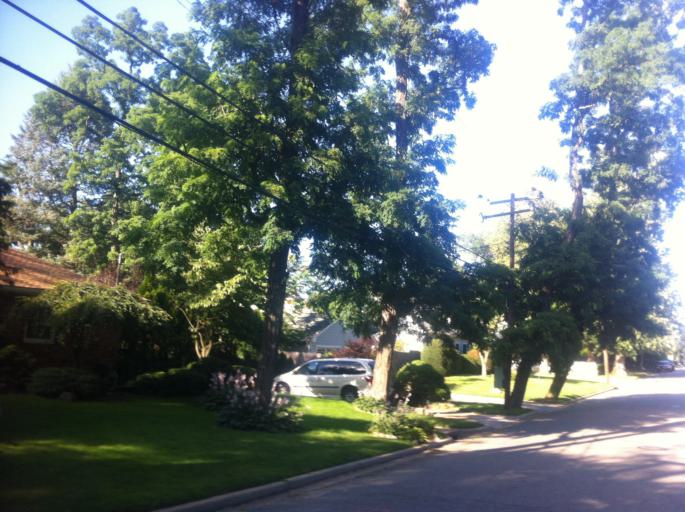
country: US
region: New York
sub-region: Nassau County
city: Lattingtown
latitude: 40.8997
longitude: -73.5831
